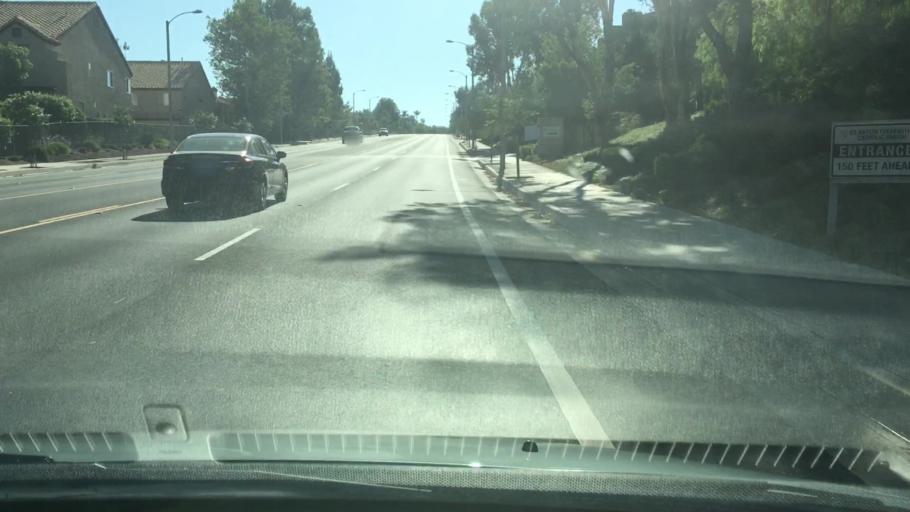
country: US
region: California
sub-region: Los Angeles County
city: Santa Clarita
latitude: 34.4601
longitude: -118.5331
